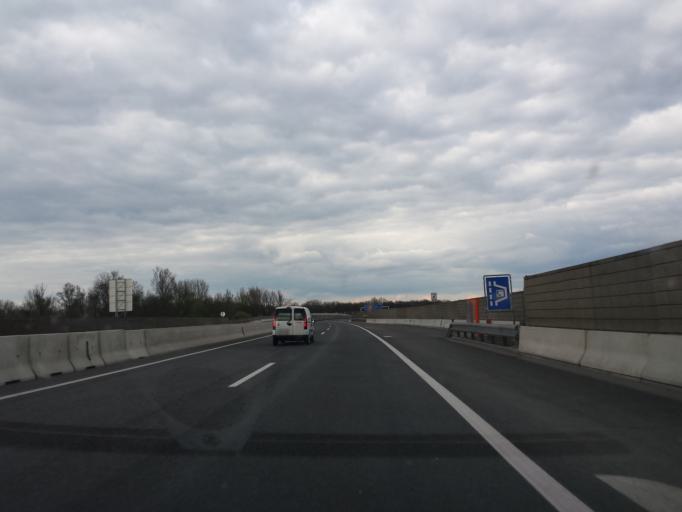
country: AT
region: Lower Austria
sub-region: Politischer Bezirk Krems
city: Grafenegg
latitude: 48.4023
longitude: 15.7384
